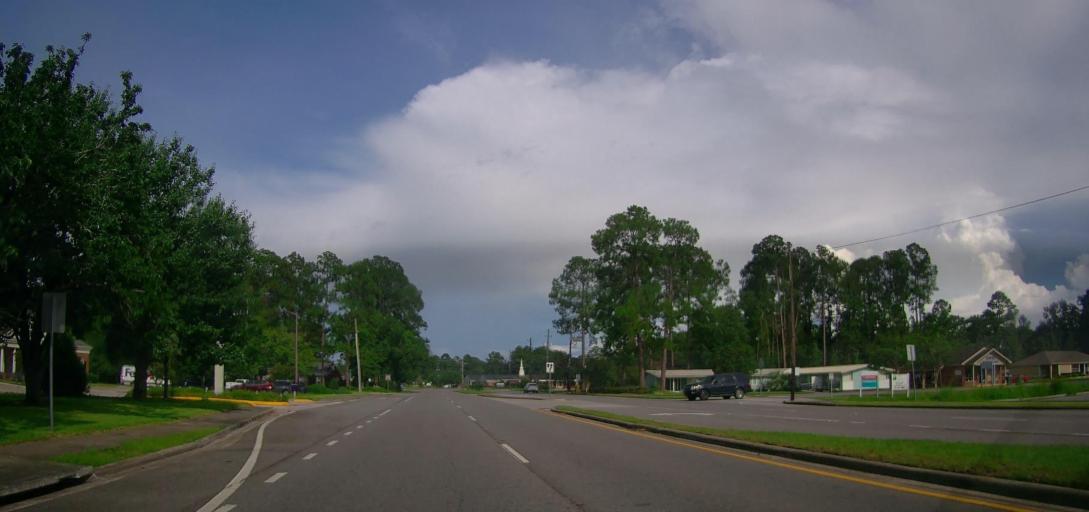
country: US
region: Georgia
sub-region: Wayne County
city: Jesup
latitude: 31.6027
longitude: -81.8980
